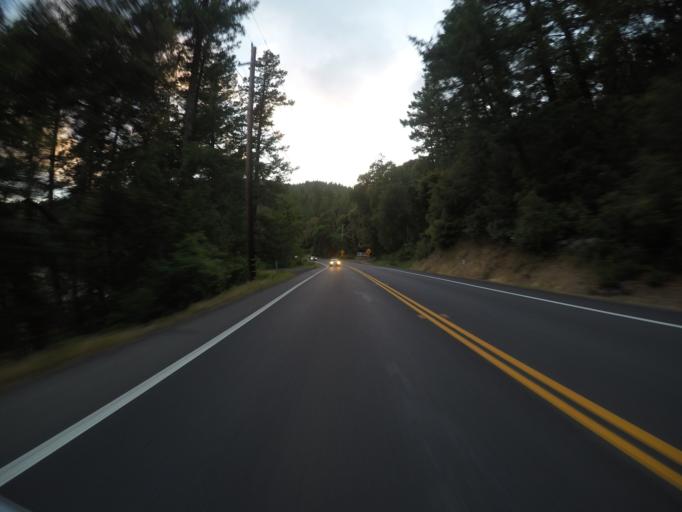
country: US
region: California
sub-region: Humboldt County
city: Redway
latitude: 40.0355
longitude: -123.7891
